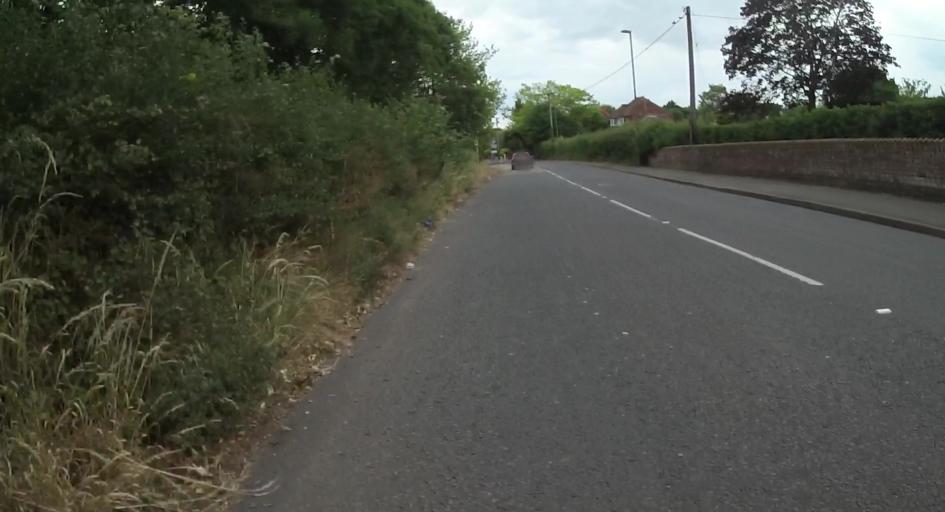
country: GB
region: England
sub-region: Surrey
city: Seale
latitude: 51.2292
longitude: -0.7326
